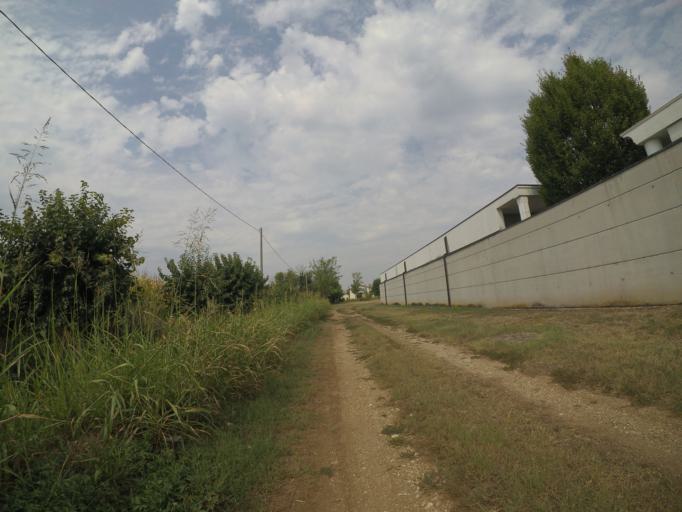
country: IT
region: Friuli Venezia Giulia
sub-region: Provincia di Udine
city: Talmassons
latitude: 45.9306
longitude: 13.1238
